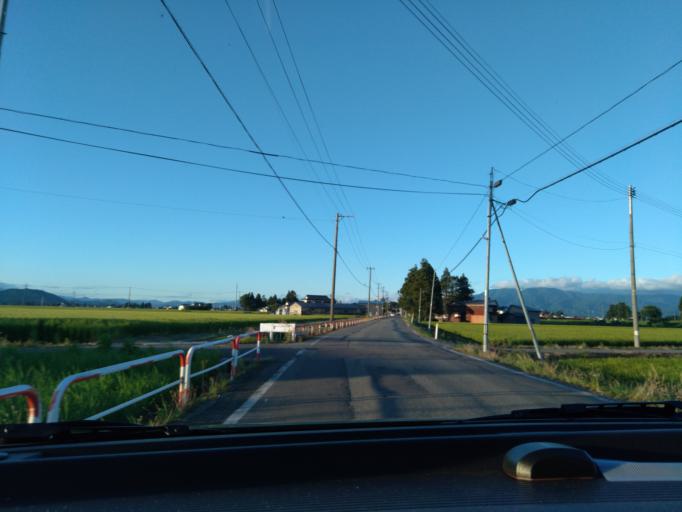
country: JP
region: Akita
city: Omagari
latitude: 39.4761
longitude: 140.5206
